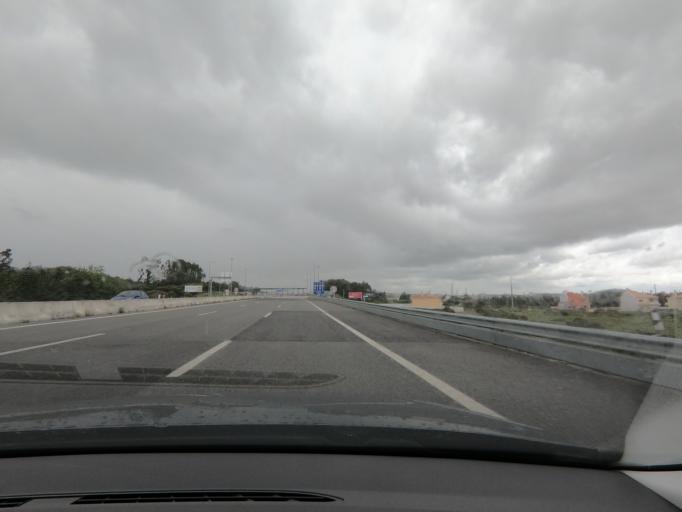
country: PT
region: Lisbon
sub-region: Sintra
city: Sintra
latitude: 38.7758
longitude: -9.3655
